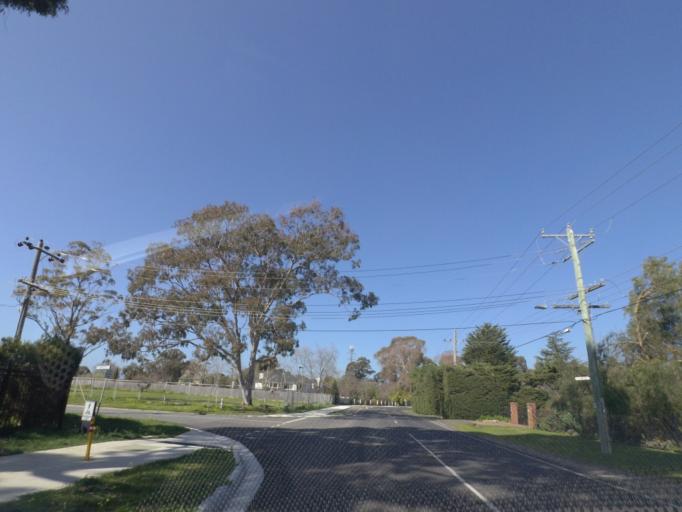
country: AU
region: Victoria
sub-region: Manningham
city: Doncaster East
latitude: -37.7655
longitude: 145.1485
